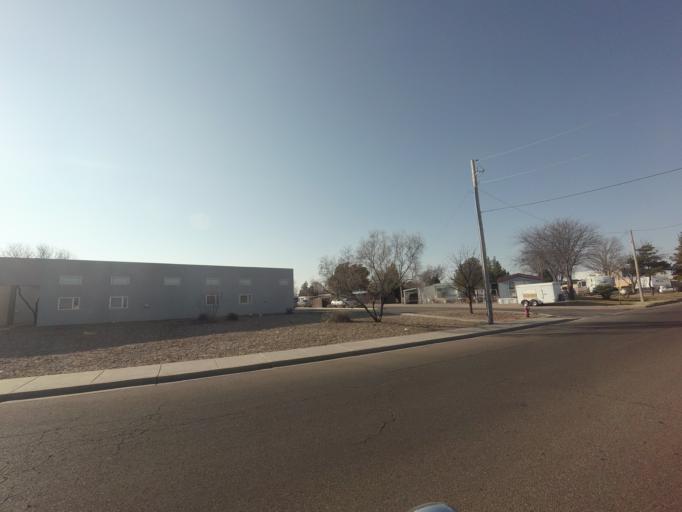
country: US
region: New Mexico
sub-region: Curry County
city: Clovis
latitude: 34.4146
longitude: -103.2080
